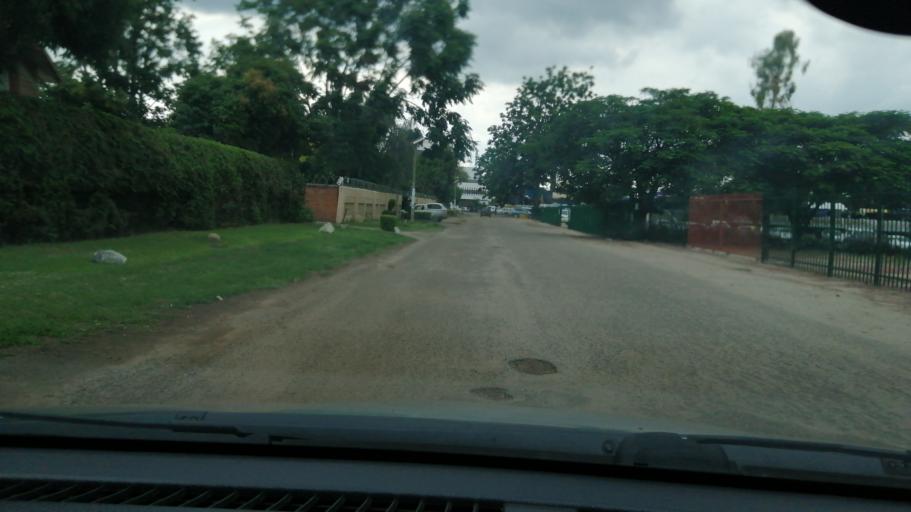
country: ZW
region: Harare
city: Harare
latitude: -17.8000
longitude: 31.0385
